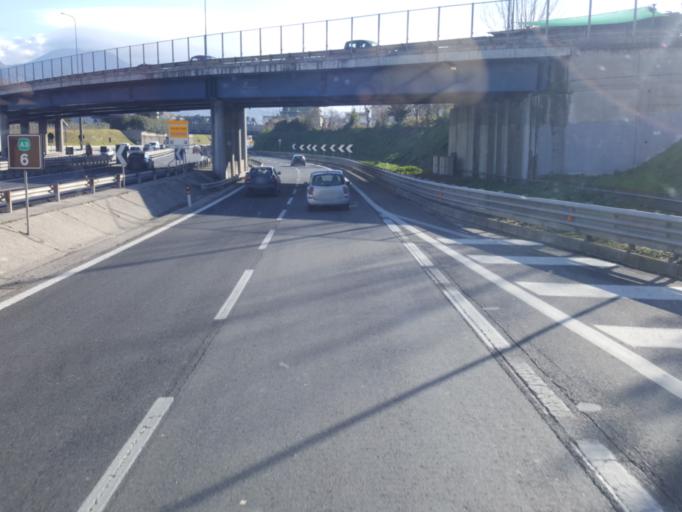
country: IT
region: Campania
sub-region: Provincia di Napoli
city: San Giorgio a Cremano
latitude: 40.8471
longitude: 14.3174
